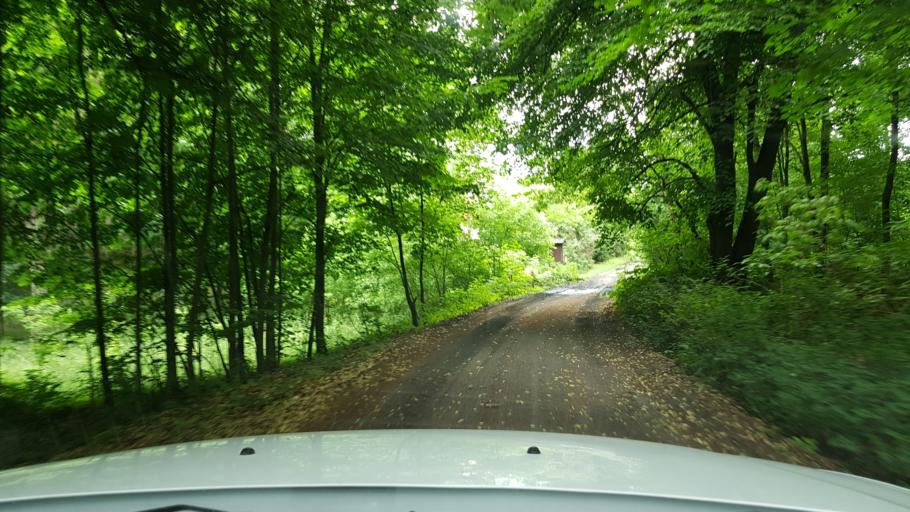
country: PL
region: West Pomeranian Voivodeship
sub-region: Powiat mysliborski
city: Boleszkowice
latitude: 52.6754
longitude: 14.5927
